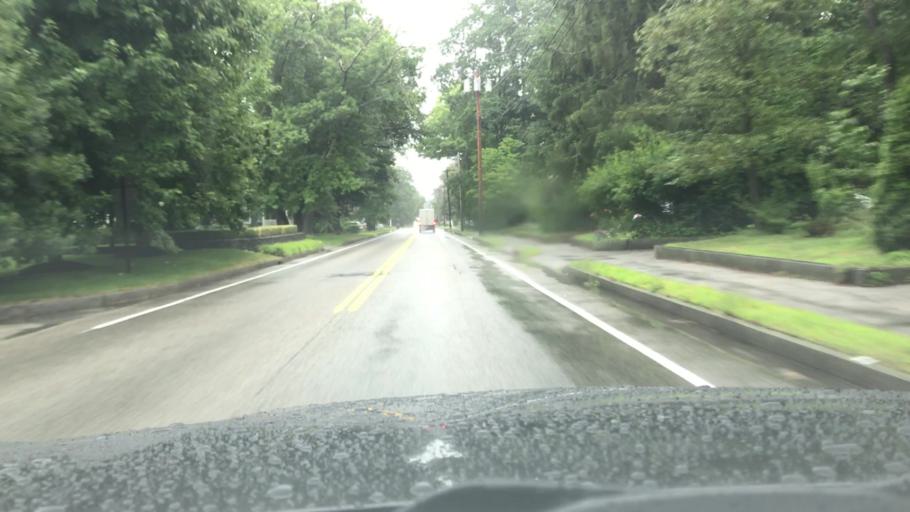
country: US
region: Maine
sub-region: York County
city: Kennebunk
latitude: 43.3902
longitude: -70.5446
